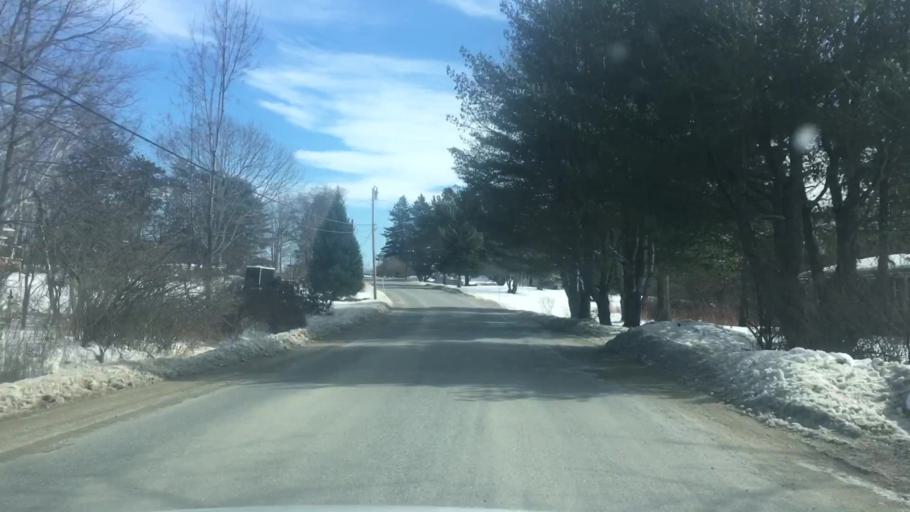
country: US
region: Maine
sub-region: Penobscot County
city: Eddington
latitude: 44.7984
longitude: -68.6770
